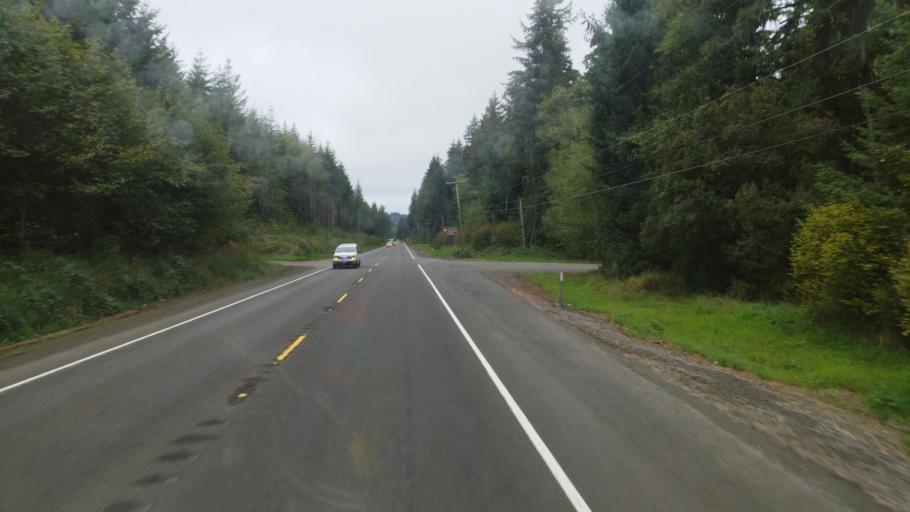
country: US
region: Washington
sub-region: Wahkiakum County
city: Cathlamet
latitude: 46.1754
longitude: -123.5041
